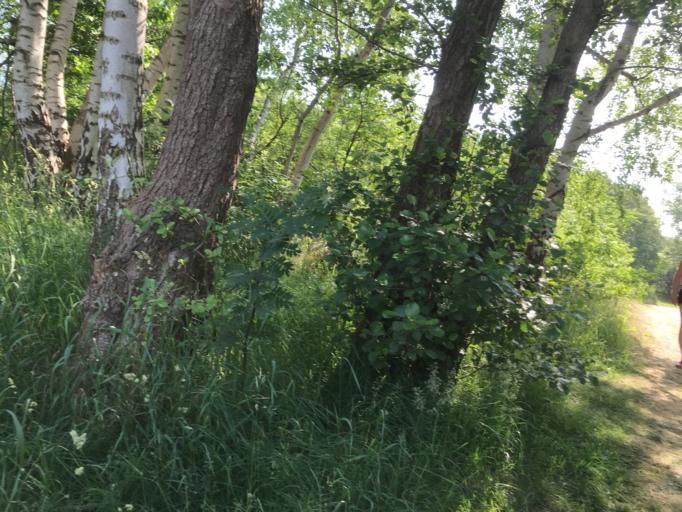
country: SE
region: Vaestra Goetaland
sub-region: Goteborg
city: Billdal
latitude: 57.6270
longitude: 11.9232
